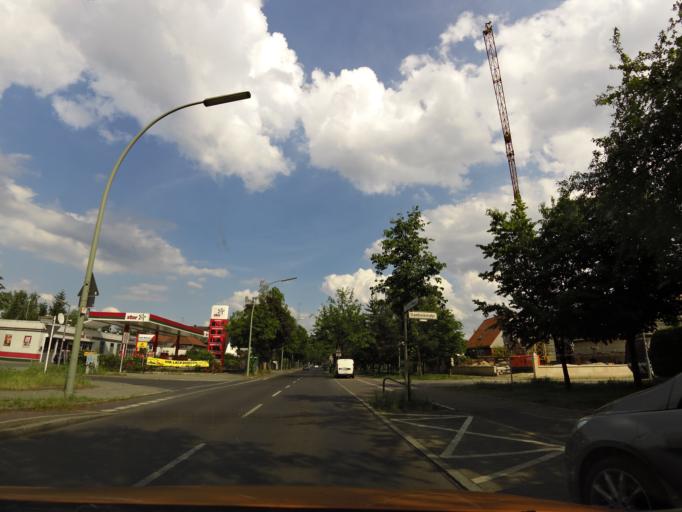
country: DE
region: Berlin
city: Heiligensee
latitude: 52.6017
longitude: 13.2425
